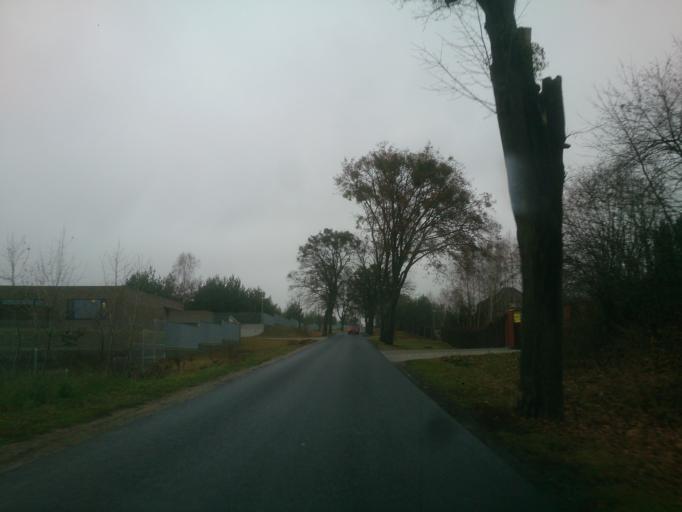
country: PL
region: Kujawsko-Pomorskie
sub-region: Powiat brodnicki
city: Brodnica
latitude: 53.2783
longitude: 19.3872
